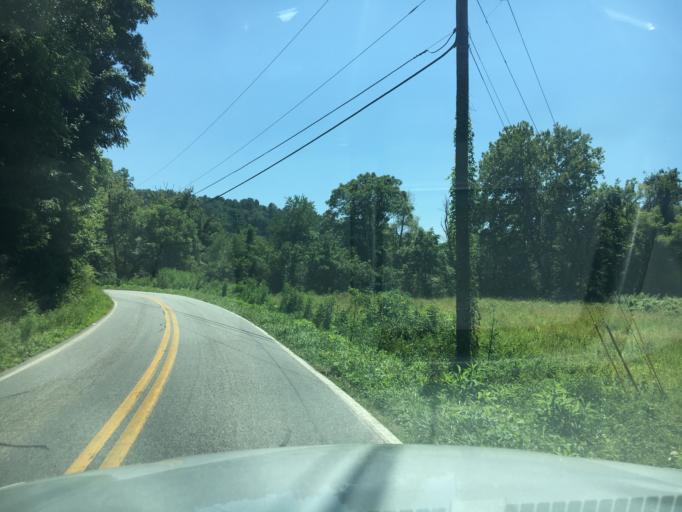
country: US
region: North Carolina
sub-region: McDowell County
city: Marion
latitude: 35.6952
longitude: -82.0444
